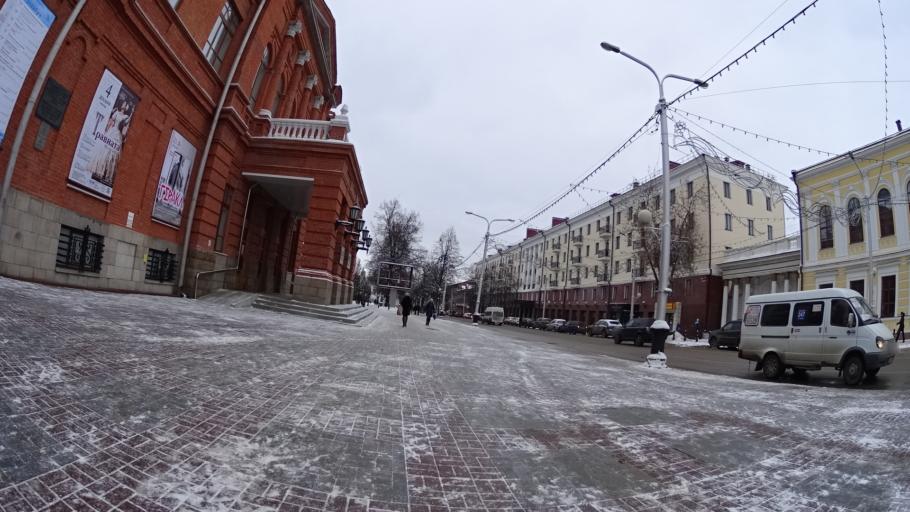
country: RU
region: Bashkortostan
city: Ufa
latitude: 54.7223
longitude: 55.9454
